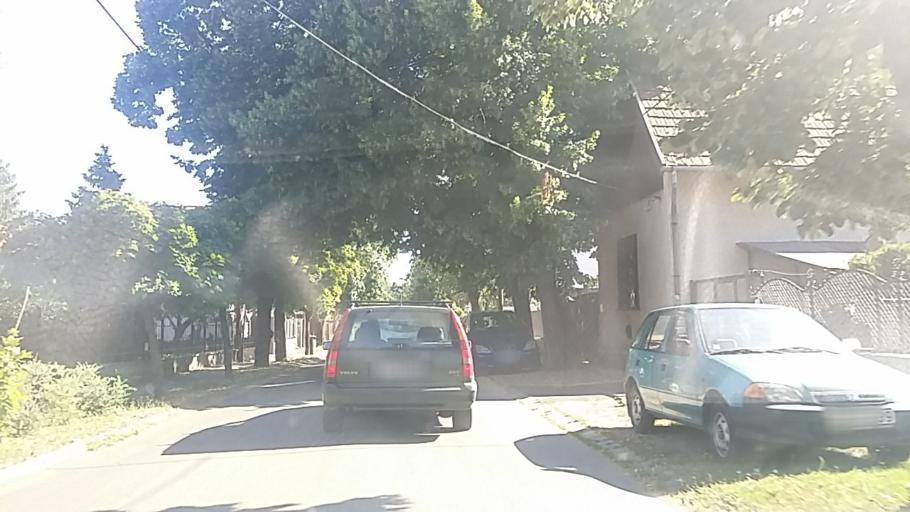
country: HU
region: Pest
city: Budakalasz
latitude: 47.5875
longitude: 19.0570
